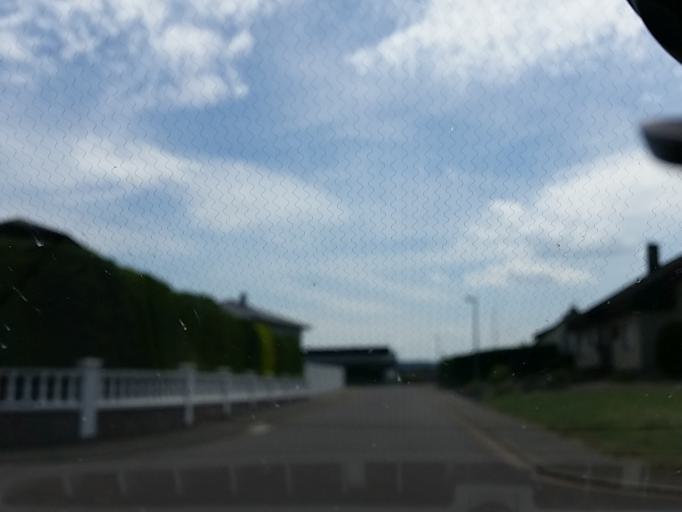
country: DE
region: Saarland
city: Schmelz
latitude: 49.4267
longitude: 6.8308
